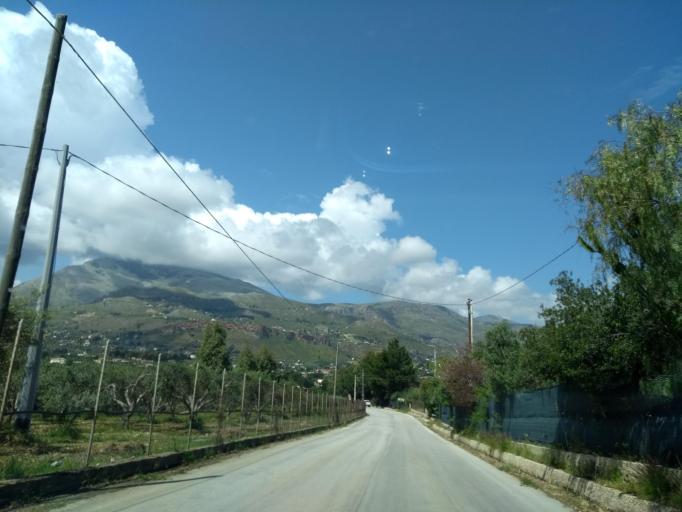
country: IT
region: Sicily
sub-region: Trapani
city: Castellammare del Golfo
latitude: 38.0450
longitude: 12.8458
